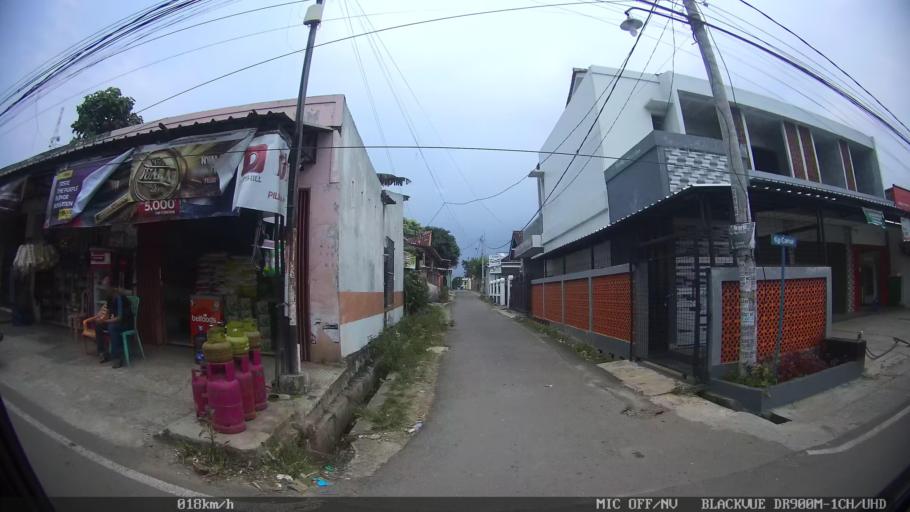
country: ID
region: Lampung
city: Kedaton
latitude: -5.3540
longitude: 105.2414
